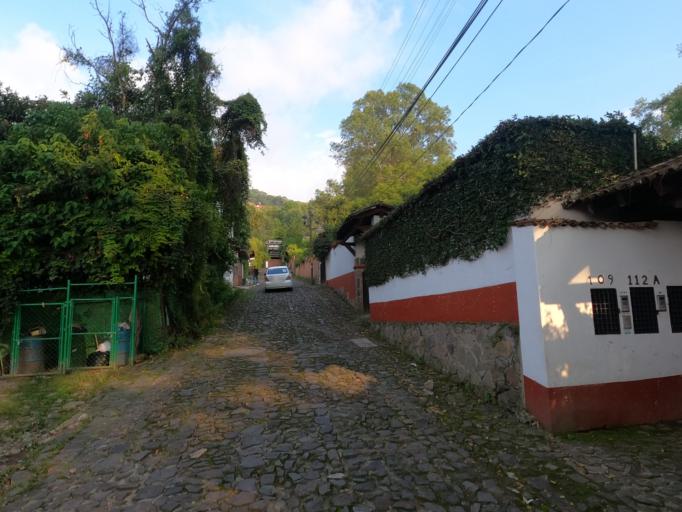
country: MX
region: Mexico
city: Valle de Bravo
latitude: 19.1969
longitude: -100.1284
